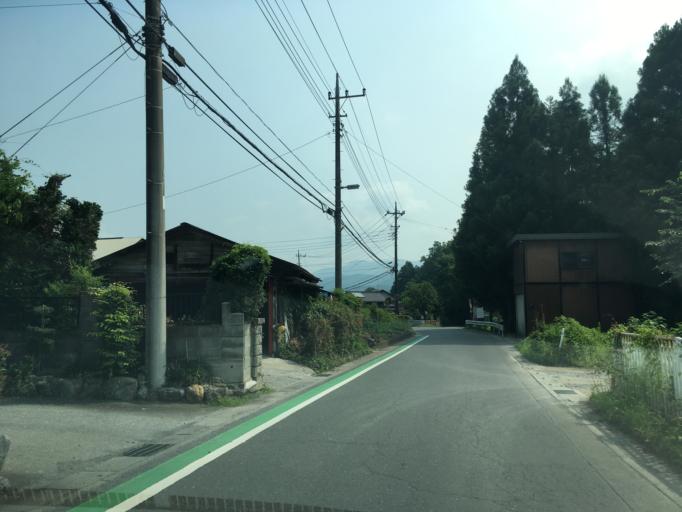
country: JP
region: Saitama
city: Chichibu
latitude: 36.0001
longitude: 139.1013
